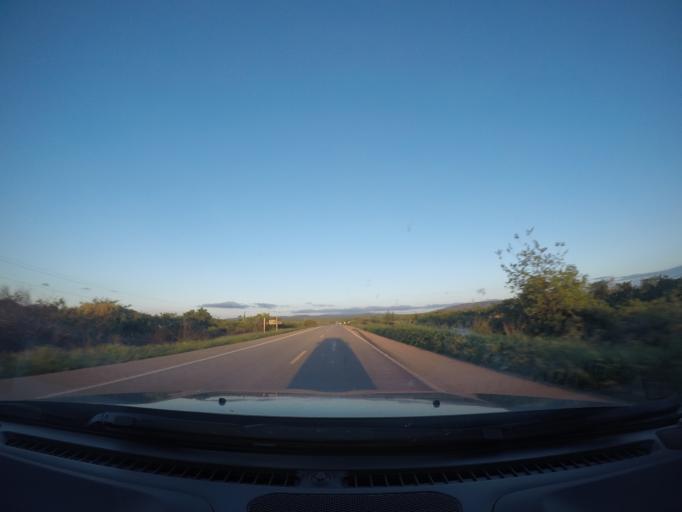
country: BR
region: Bahia
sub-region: Seabra
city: Seabra
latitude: -12.4000
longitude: -41.9426
